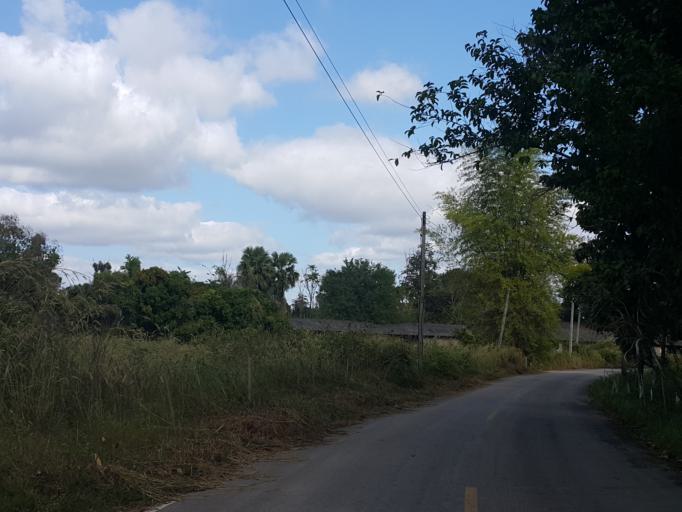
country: TH
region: Lampang
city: Hang Chat
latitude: 18.3470
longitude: 99.3641
